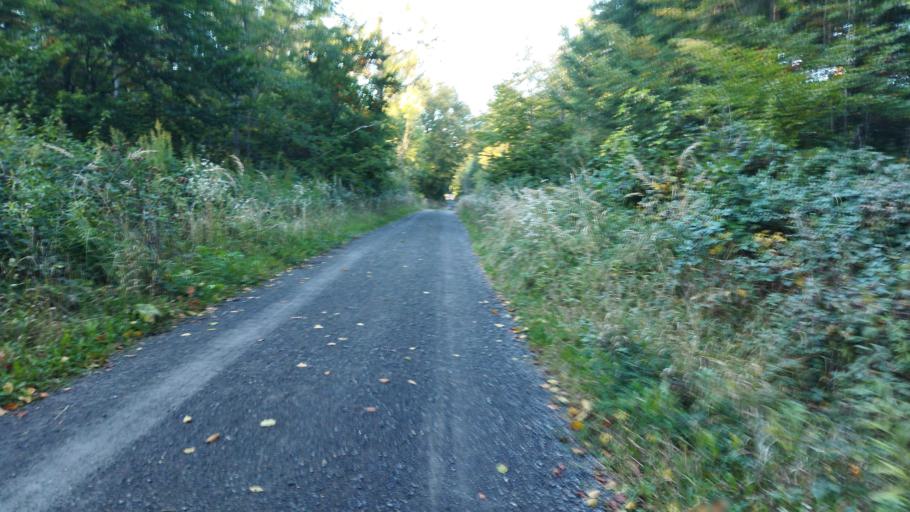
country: DE
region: Baden-Wuerttemberg
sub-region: Regierungsbezirk Stuttgart
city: Cleebronn
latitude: 49.0165
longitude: 9.0265
